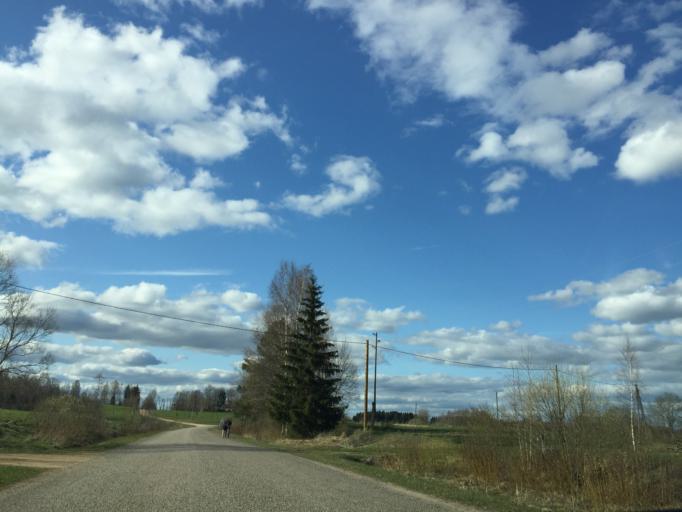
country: LV
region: Rezekne
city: Rezekne
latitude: 56.6276
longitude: 27.3072
